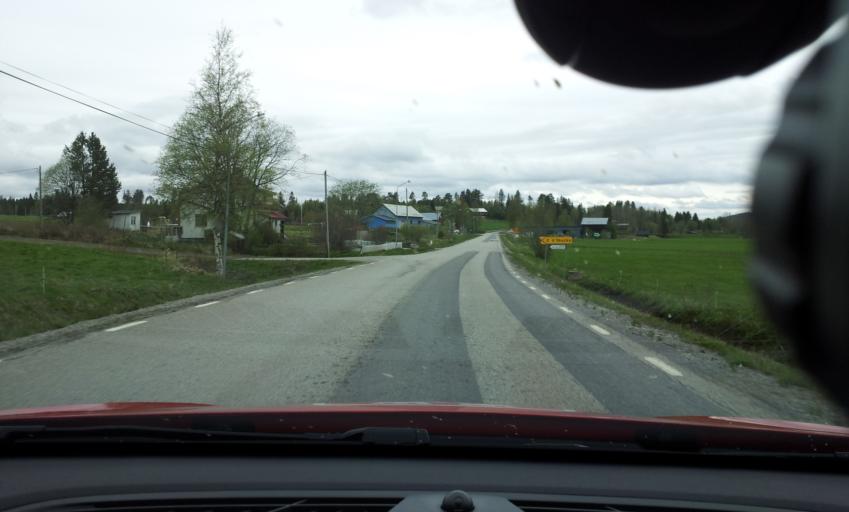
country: SE
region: Jaemtland
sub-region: Bergs Kommun
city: Hoverberg
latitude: 62.7739
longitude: 14.5265
